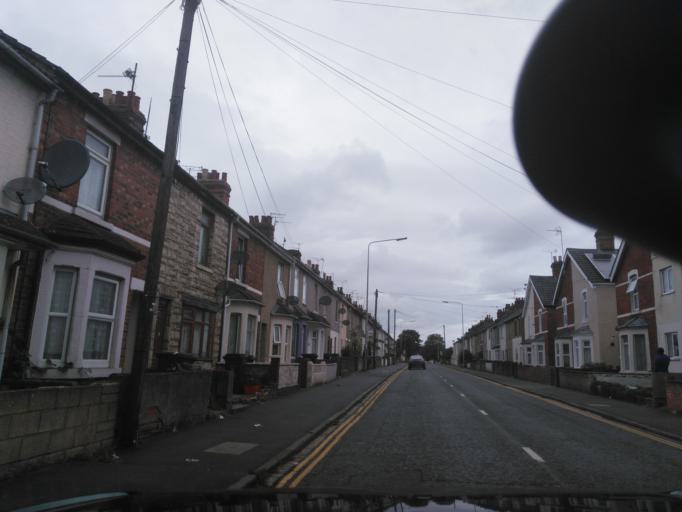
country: GB
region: England
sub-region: Borough of Swindon
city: Swindon
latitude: 51.5716
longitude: -1.7857
